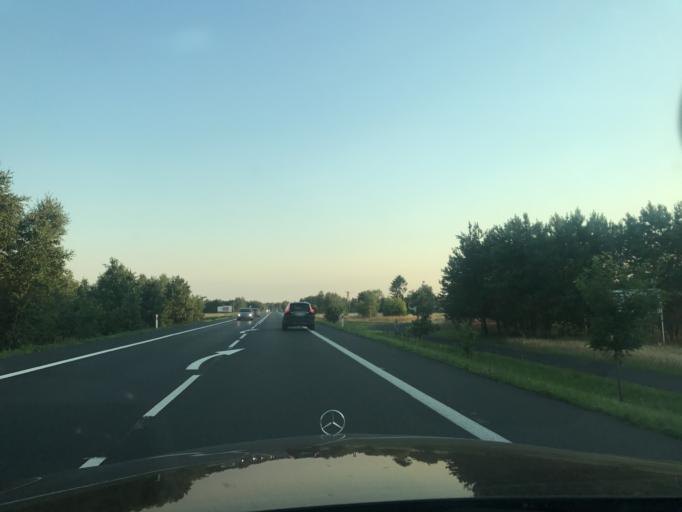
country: PL
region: Lublin Voivodeship
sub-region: Powiat lubartowski
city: Lubartow
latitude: 51.4703
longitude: 22.5826
